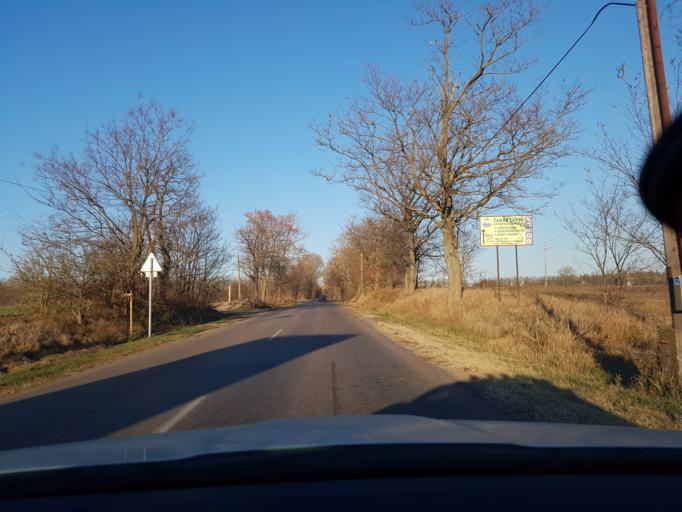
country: HU
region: Bacs-Kiskun
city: Lajosmizse
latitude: 47.0426
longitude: 19.5724
